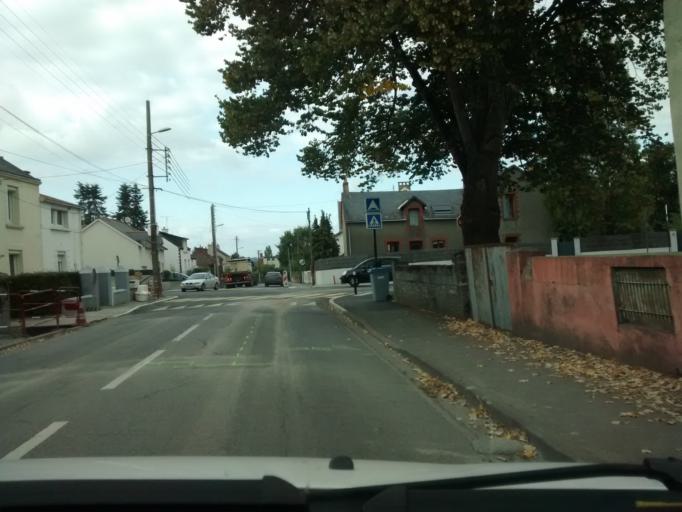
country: FR
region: Pays de la Loire
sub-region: Departement de la Loire-Atlantique
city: Coueron
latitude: 47.2173
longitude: -1.7253
